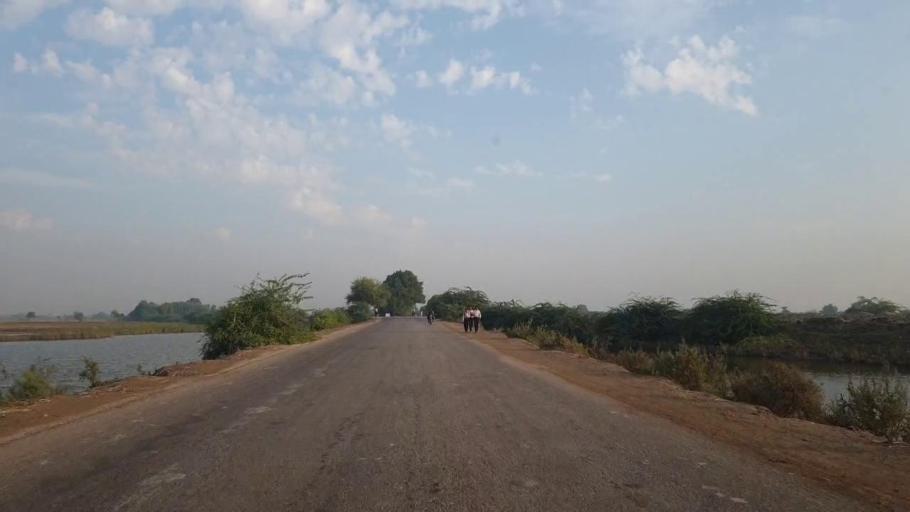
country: PK
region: Sindh
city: Tando Bago
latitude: 24.7141
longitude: 68.9391
